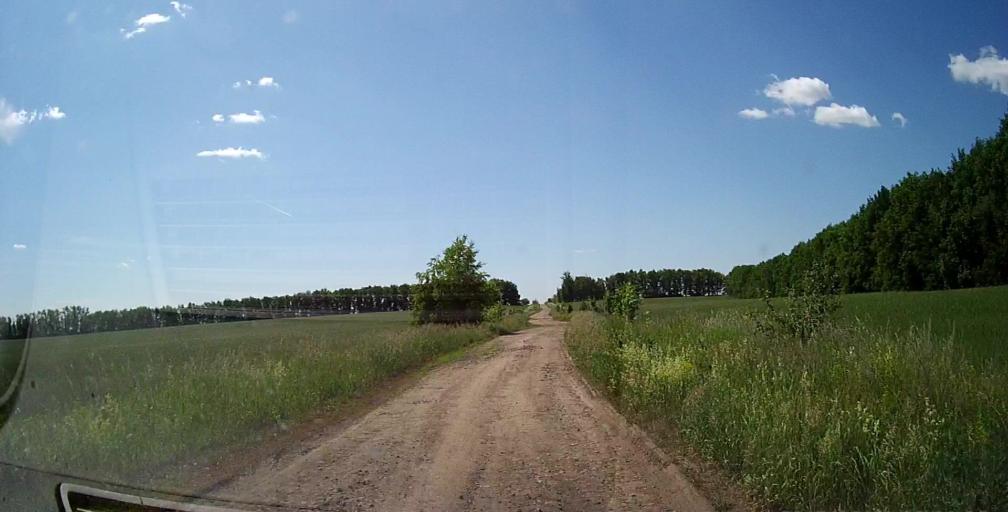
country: RU
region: Tula
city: Kurkino
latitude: 53.1826
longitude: 38.4847
